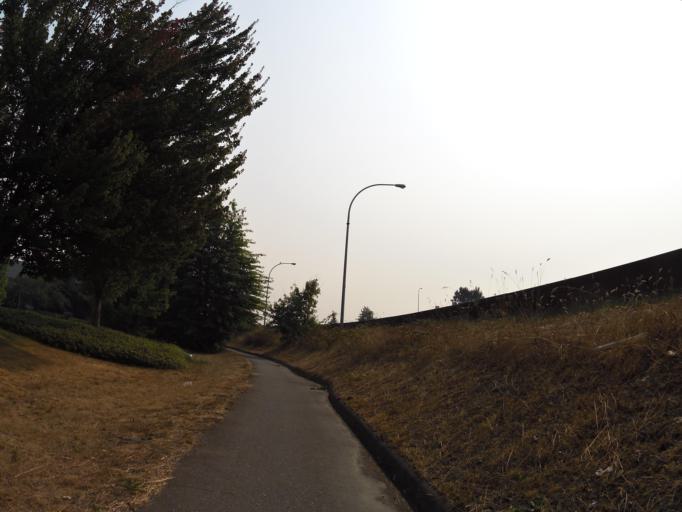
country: CA
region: British Columbia
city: New Westminster
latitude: 49.1726
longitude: -122.9520
